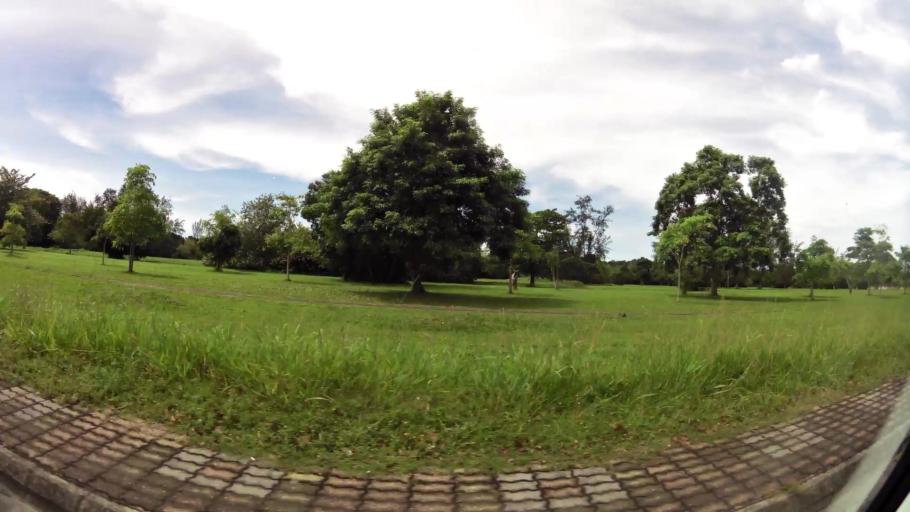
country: BN
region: Belait
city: Seria
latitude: 4.6042
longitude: 114.2958
